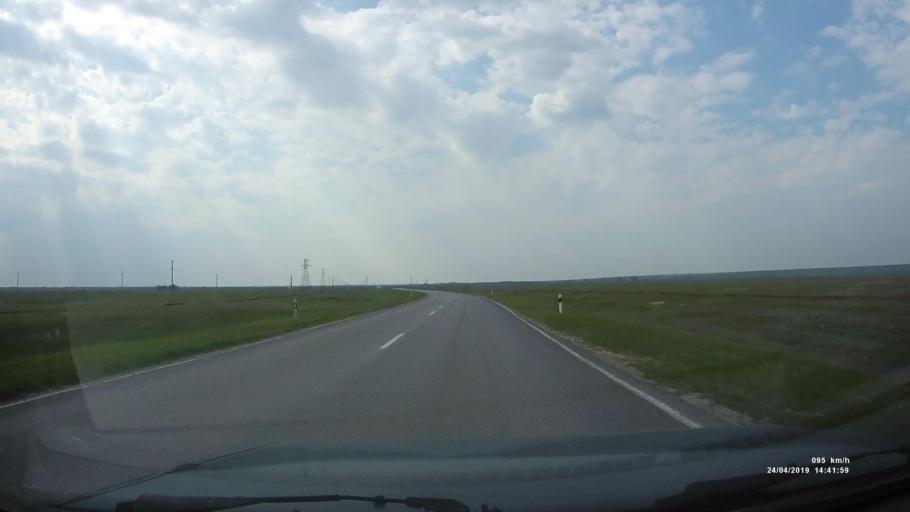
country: RU
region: Rostov
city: Remontnoye
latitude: 46.4499
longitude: 43.8700
